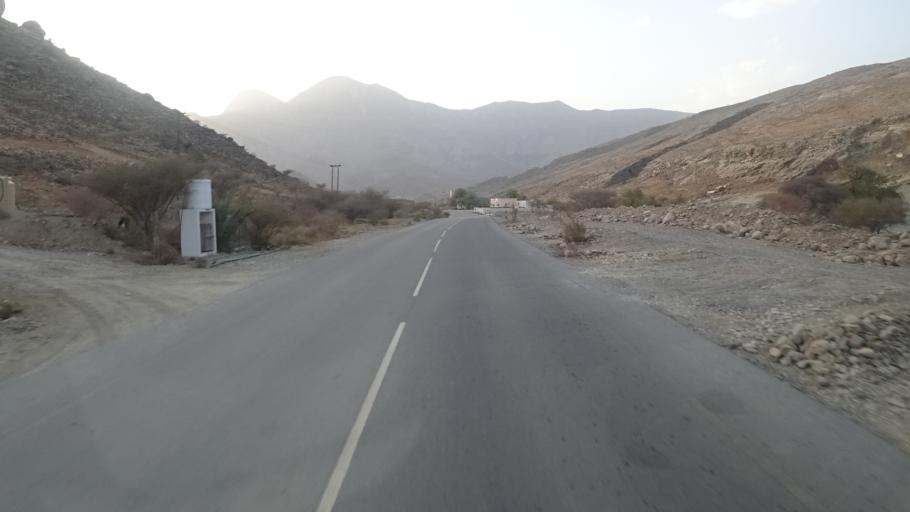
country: OM
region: Muhafazat ad Dakhiliyah
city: Bahla'
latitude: 23.1681
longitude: 57.1577
